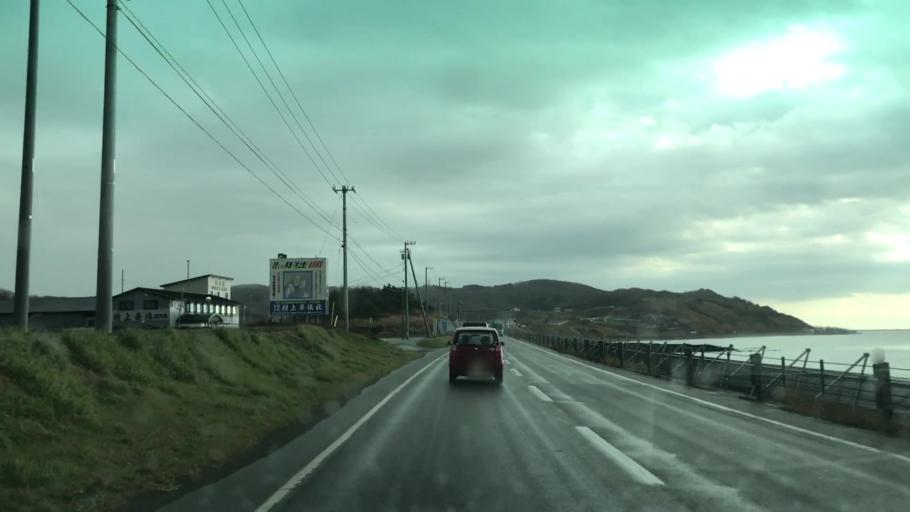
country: JP
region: Hokkaido
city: Shizunai-furukawacho
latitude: 42.1866
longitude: 142.7130
